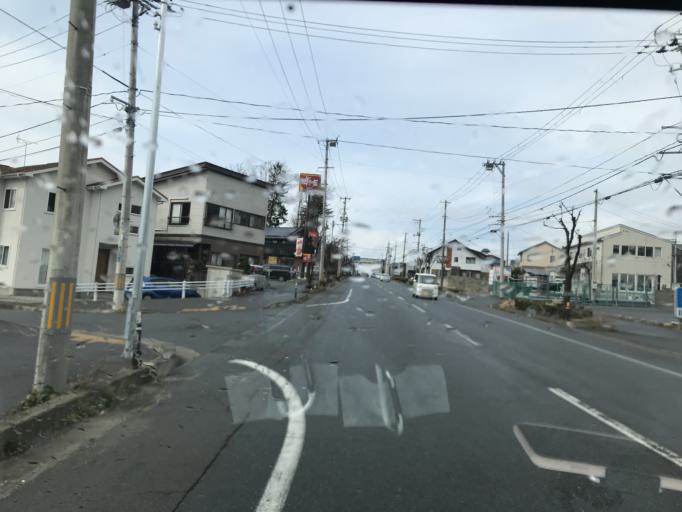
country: JP
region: Iwate
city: Kitakami
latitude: 39.2981
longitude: 141.1181
